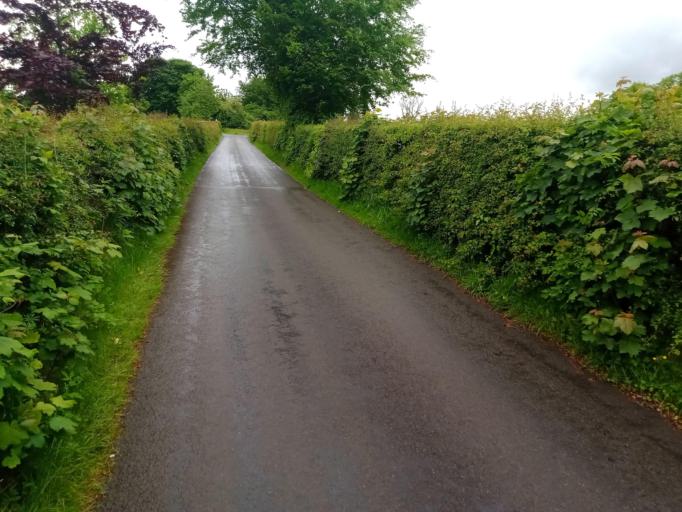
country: IE
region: Leinster
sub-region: Kilkenny
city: Thomastown
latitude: 52.4779
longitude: -7.0602
